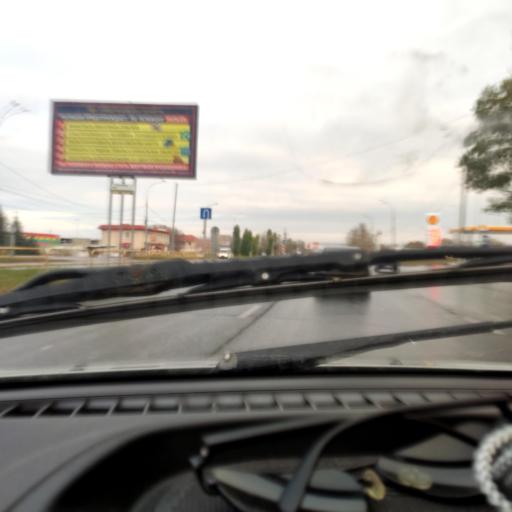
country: RU
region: Samara
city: Tol'yatti
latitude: 53.5417
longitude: 49.2849
